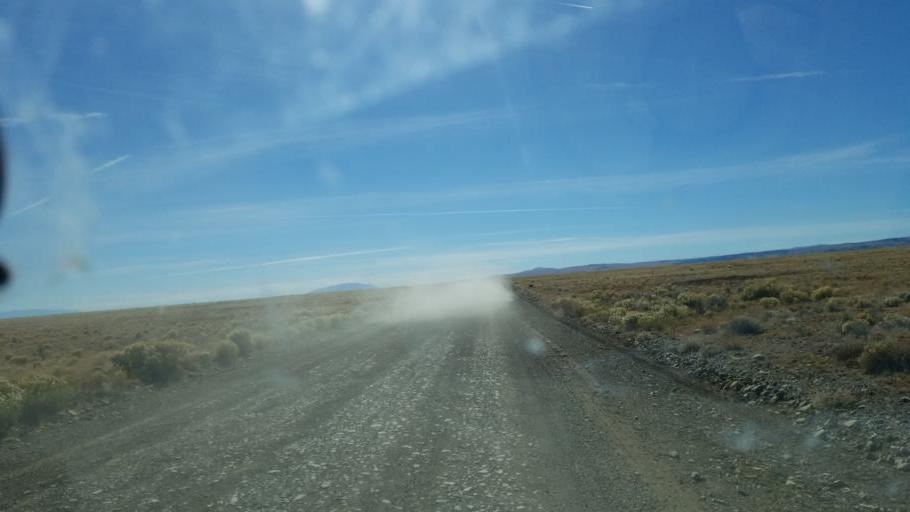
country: US
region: Colorado
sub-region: Rio Grande County
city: Monte Vista
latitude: 37.3495
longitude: -106.1491
